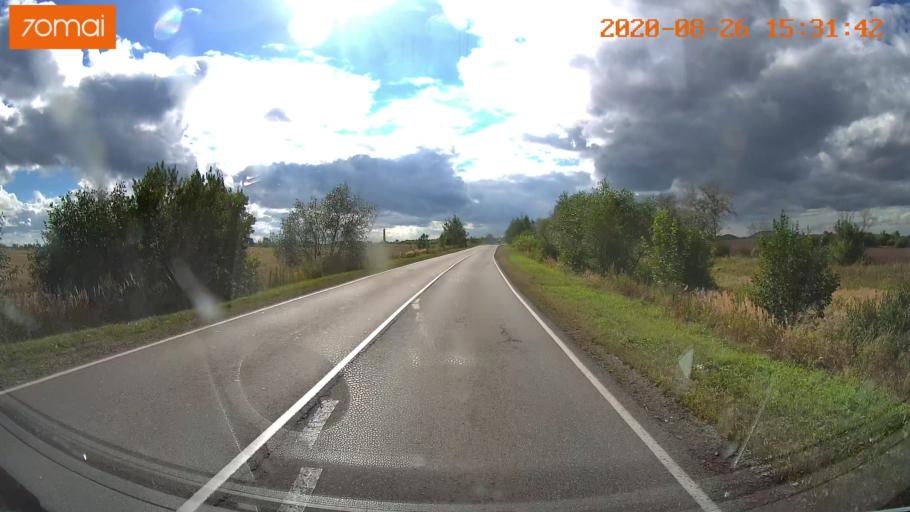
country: RU
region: Tula
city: Severo-Zadonsk
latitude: 54.0771
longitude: 38.3818
